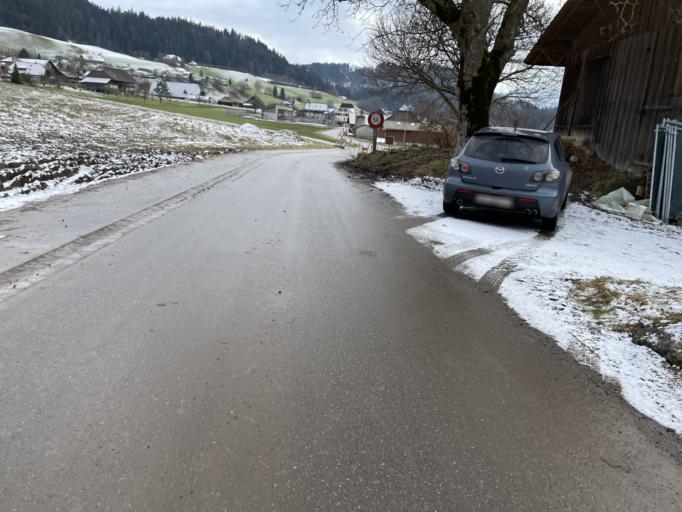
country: CH
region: Lucerne
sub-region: Entlebuch District
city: Oberdiessbach
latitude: 46.8206
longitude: 7.6134
